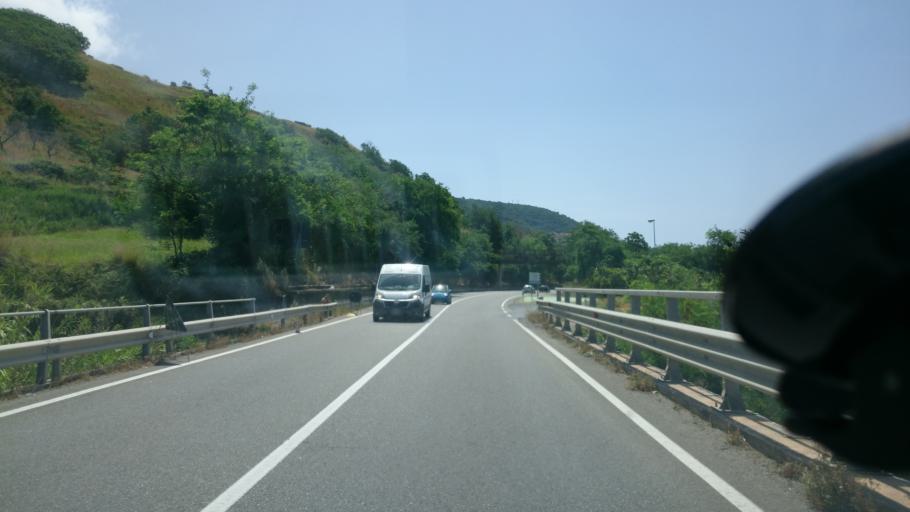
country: IT
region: Calabria
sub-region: Provincia di Cosenza
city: Cittadella del Capo
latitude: 39.5675
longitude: 15.8738
